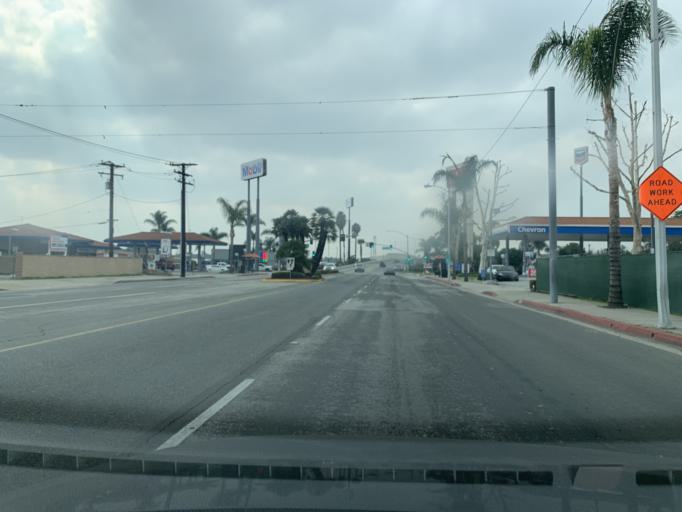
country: US
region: California
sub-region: Los Angeles County
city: South El Monte
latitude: 34.0417
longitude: -118.0493
